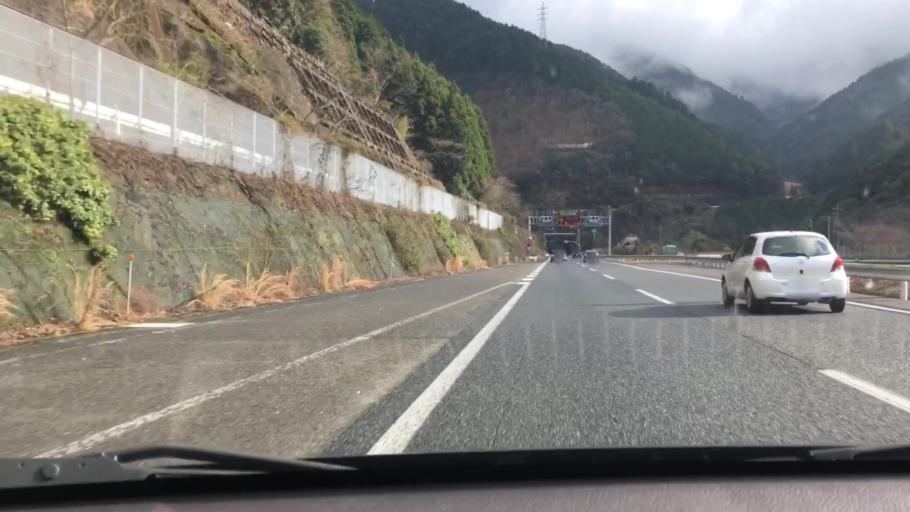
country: JP
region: Kumamoto
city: Yatsushiro
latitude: 32.3964
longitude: 130.7043
